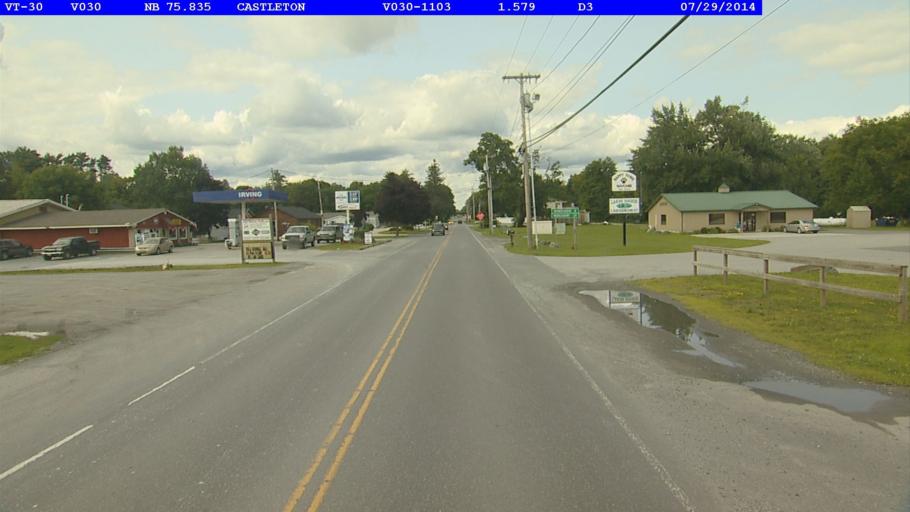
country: US
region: Vermont
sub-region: Rutland County
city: Castleton
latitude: 43.6095
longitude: -73.2082
